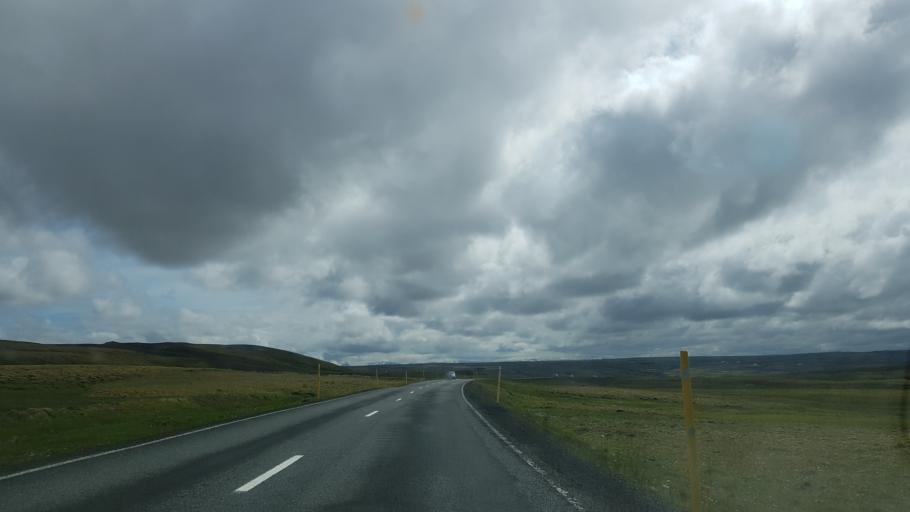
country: IS
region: West
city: Borgarnes
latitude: 64.9644
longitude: -21.0620
